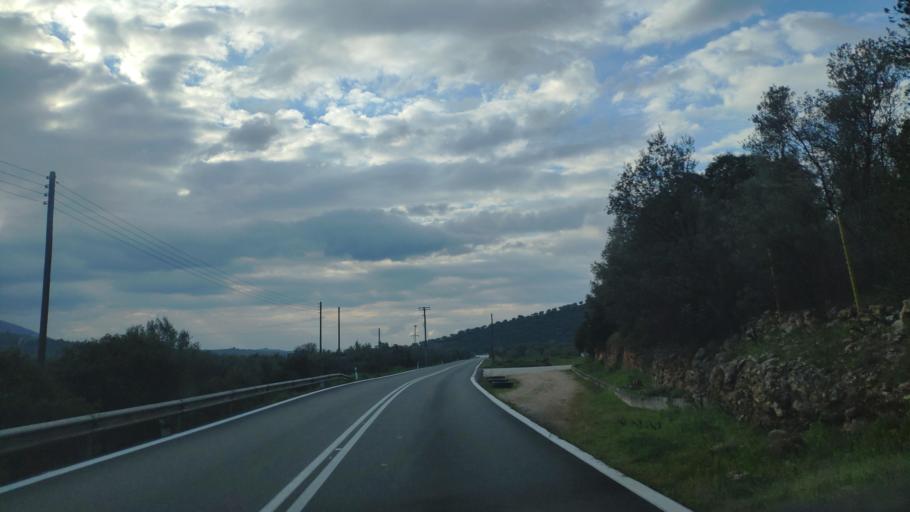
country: GR
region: Peloponnese
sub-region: Nomos Argolidos
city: Koutsopodi
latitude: 37.7455
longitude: 22.7344
